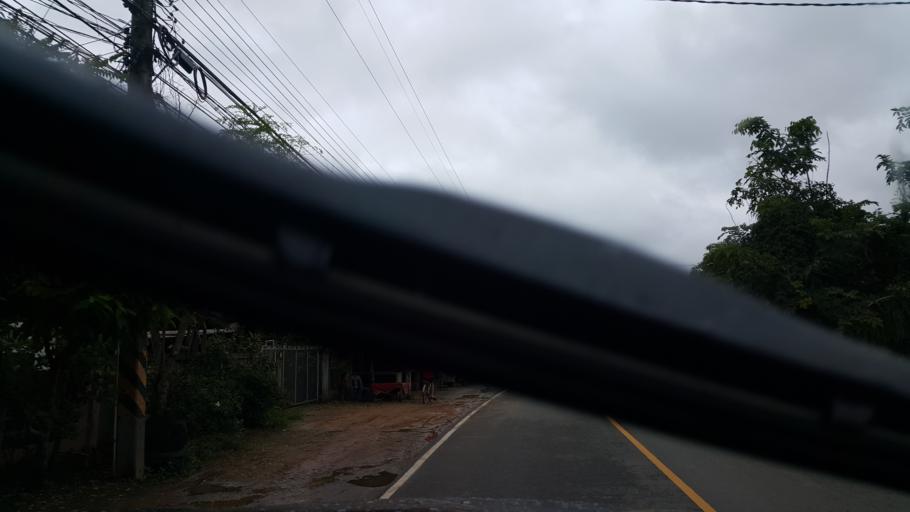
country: TH
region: Phayao
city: Chiang Kham
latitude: 19.5231
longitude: 100.3498
